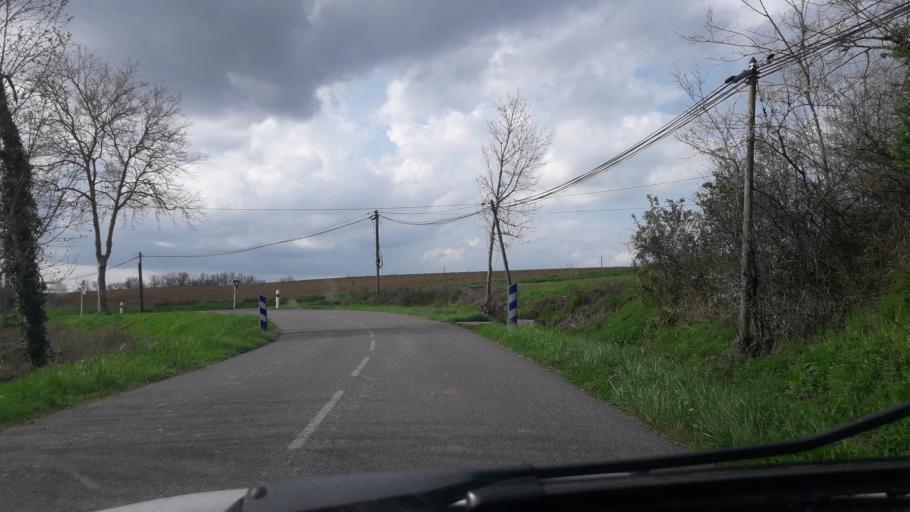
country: FR
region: Midi-Pyrenees
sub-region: Departement de la Haute-Garonne
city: Rieux-Volvestre
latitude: 43.2599
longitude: 1.2327
